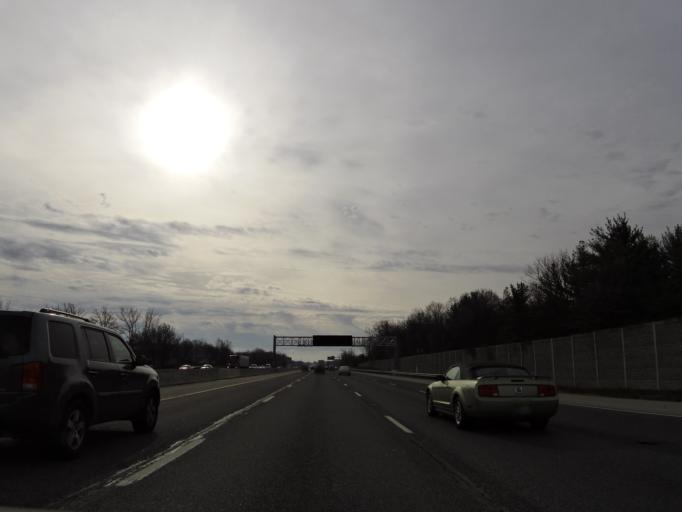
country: US
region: Indiana
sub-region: Marion County
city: Lawrence
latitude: 39.8785
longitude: -86.0476
